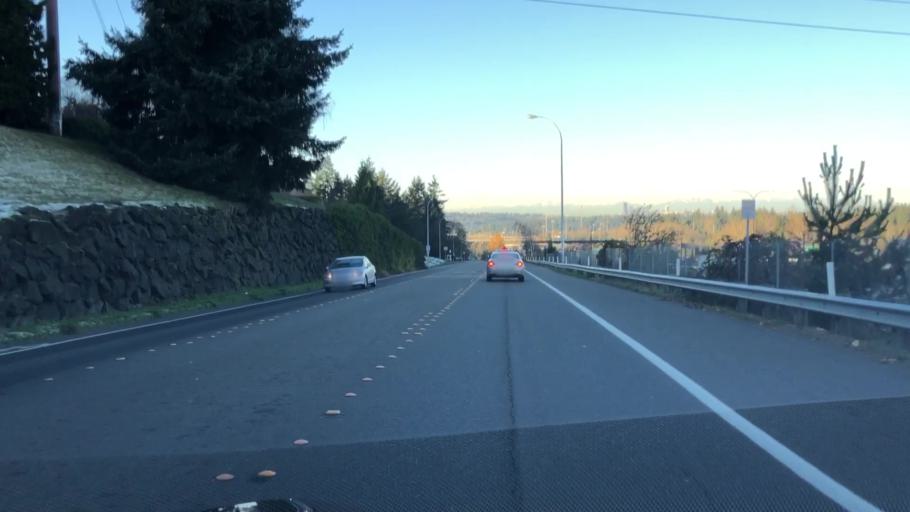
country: US
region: Washington
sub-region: King County
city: Eastgate
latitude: 47.5794
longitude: -122.1572
